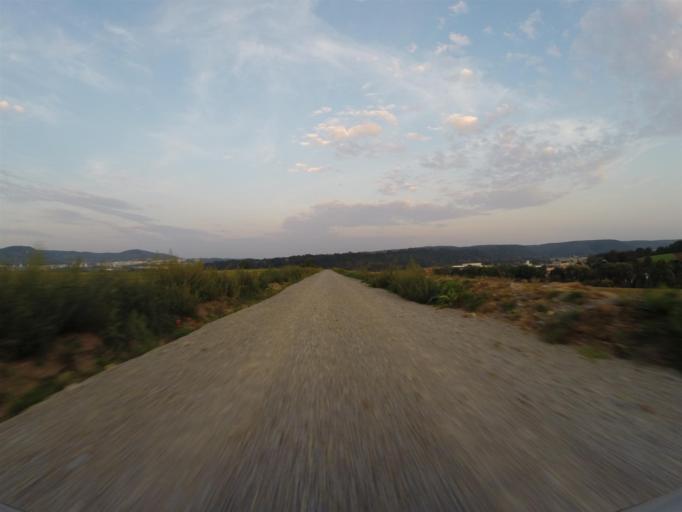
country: DE
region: Thuringia
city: Rothenstein
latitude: 50.8696
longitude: 11.5926
